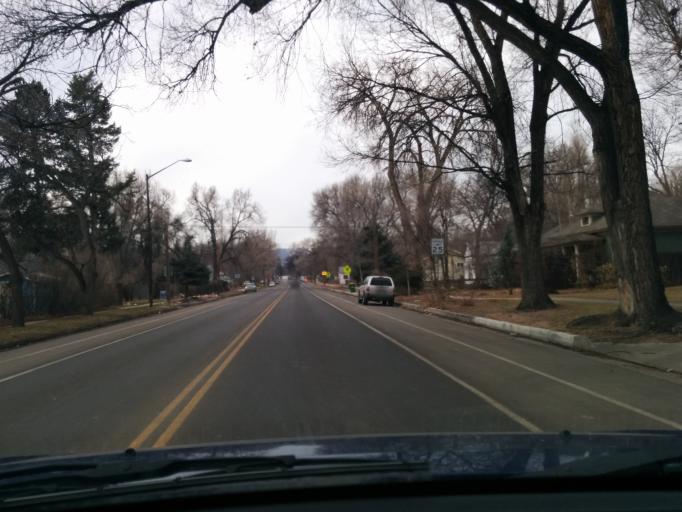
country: US
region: Colorado
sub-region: Larimer County
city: Fort Collins
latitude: 40.5922
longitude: -105.0861
